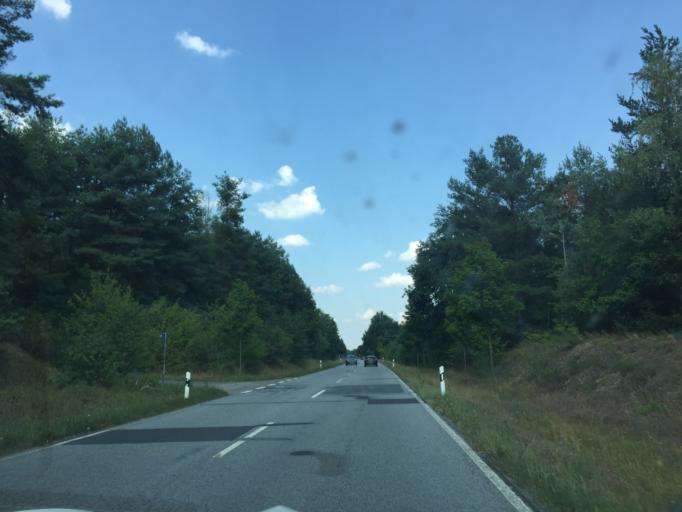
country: DE
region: Saxony
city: Boxberg
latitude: 51.4358
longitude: 14.5238
